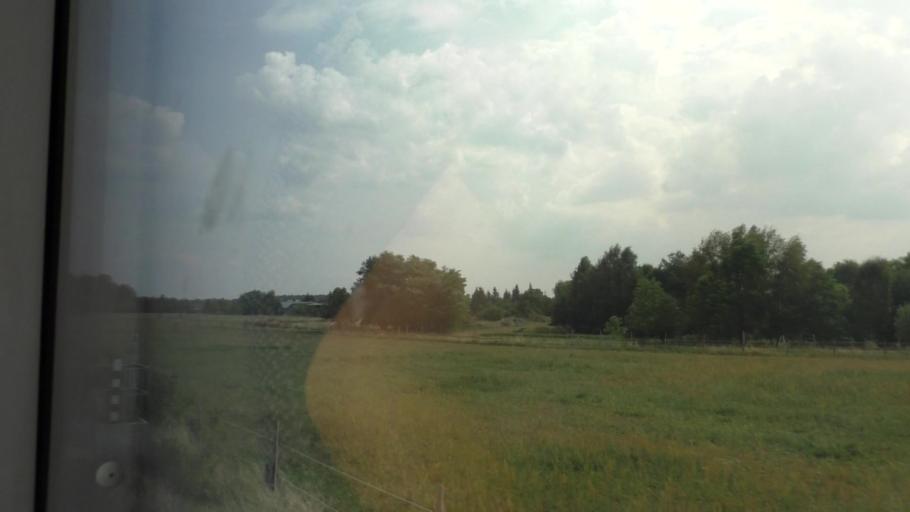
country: DE
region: Brandenburg
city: Tauche
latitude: 52.1747
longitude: 14.1995
